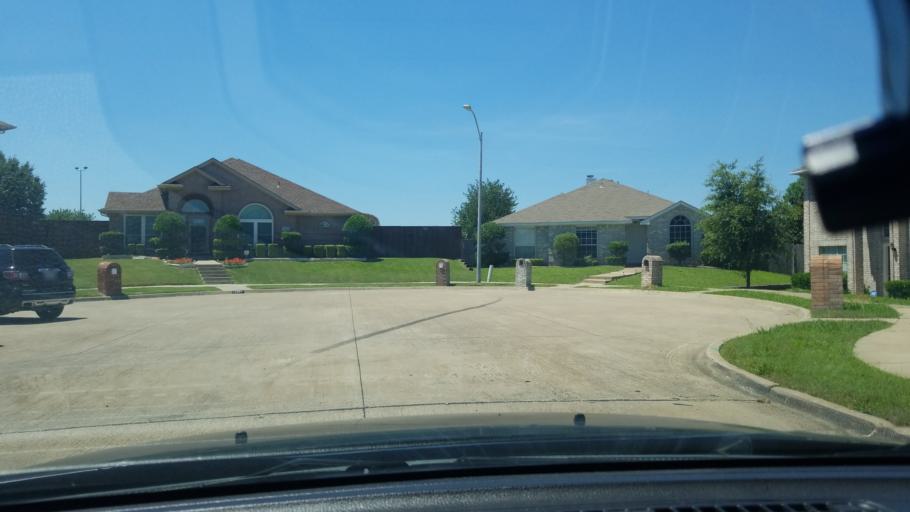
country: US
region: Texas
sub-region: Dallas County
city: Mesquite
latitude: 32.7531
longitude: -96.6115
